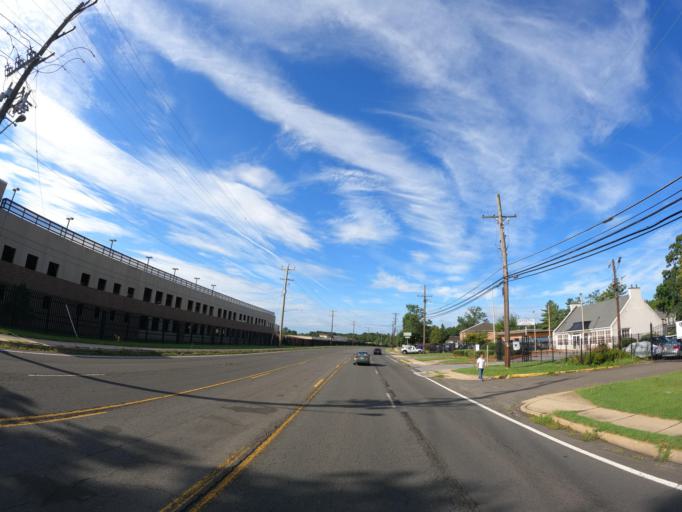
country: US
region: Maryland
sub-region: Prince George's County
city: Camp Springs
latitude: 38.8109
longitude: -76.8961
